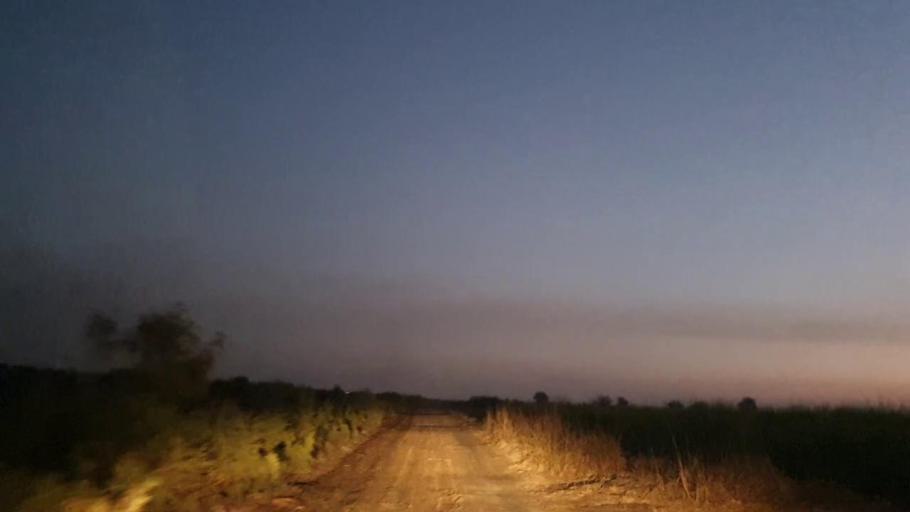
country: PK
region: Sindh
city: Nawabshah
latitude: 26.3276
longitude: 68.3765
